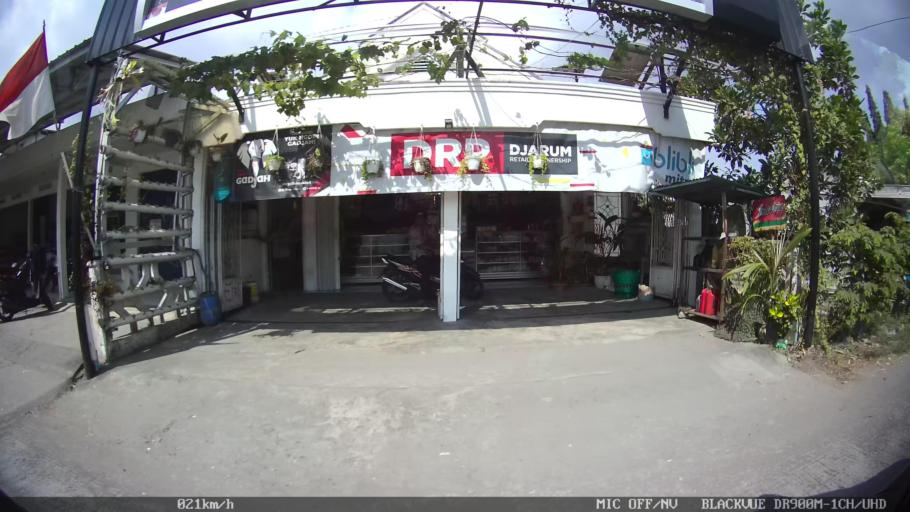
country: ID
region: Daerah Istimewa Yogyakarta
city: Kasihan
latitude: -7.8175
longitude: 110.3283
